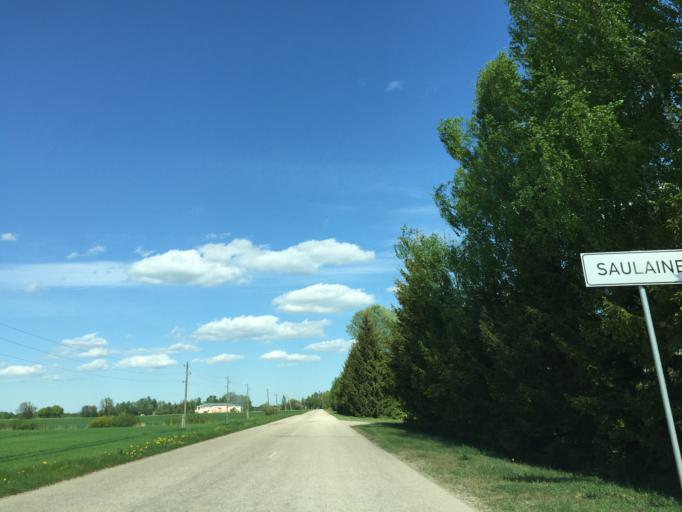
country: LV
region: Bauskas Rajons
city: Bauska
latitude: 56.3944
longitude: 24.1147
